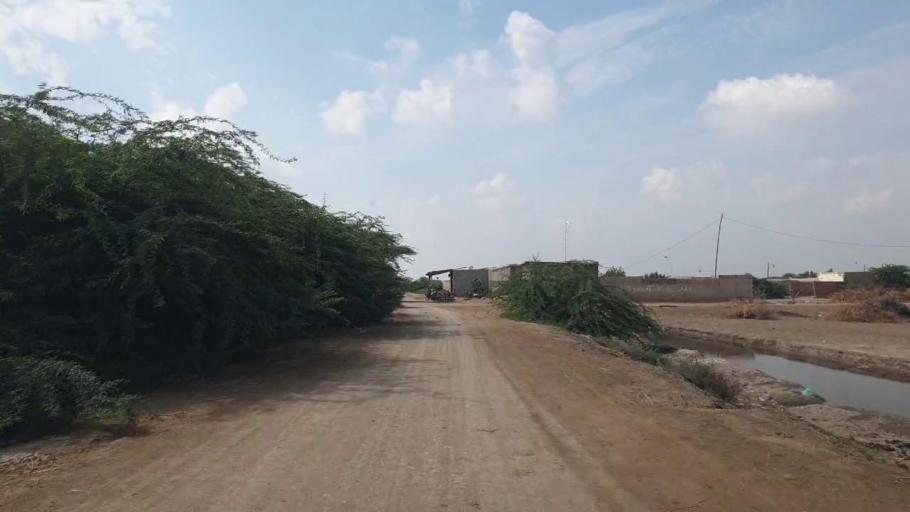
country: PK
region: Sindh
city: Badin
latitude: 24.5066
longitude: 68.6444
